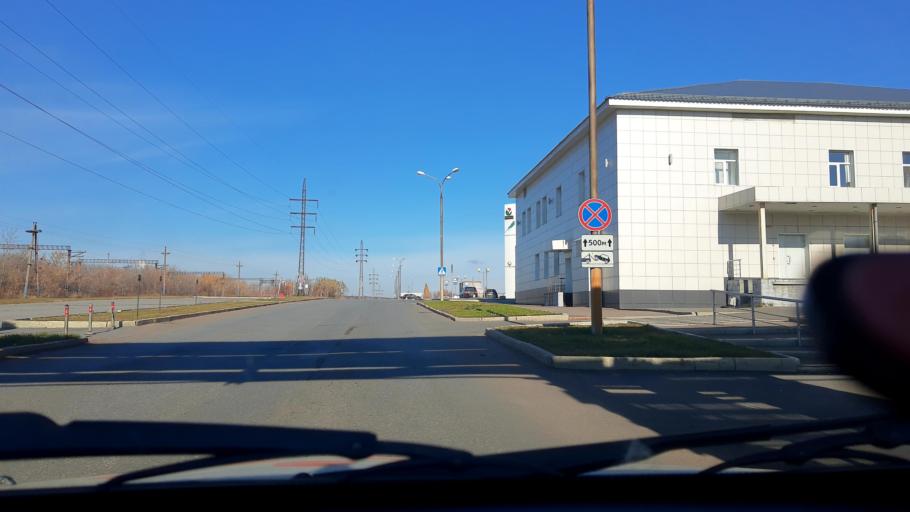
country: RU
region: Bashkortostan
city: Ufa
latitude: 54.8757
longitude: 56.1010
